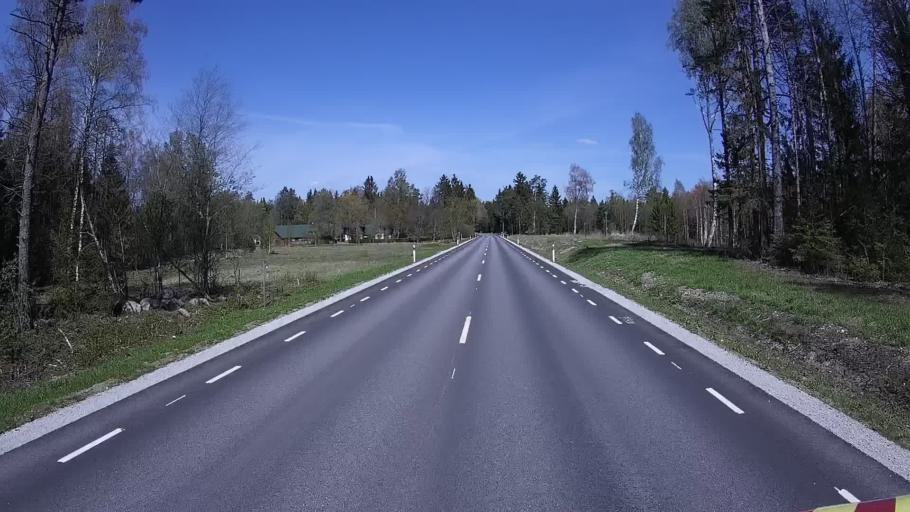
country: EE
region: Harju
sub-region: Nissi vald
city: Turba
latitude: 59.1445
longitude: 24.0772
